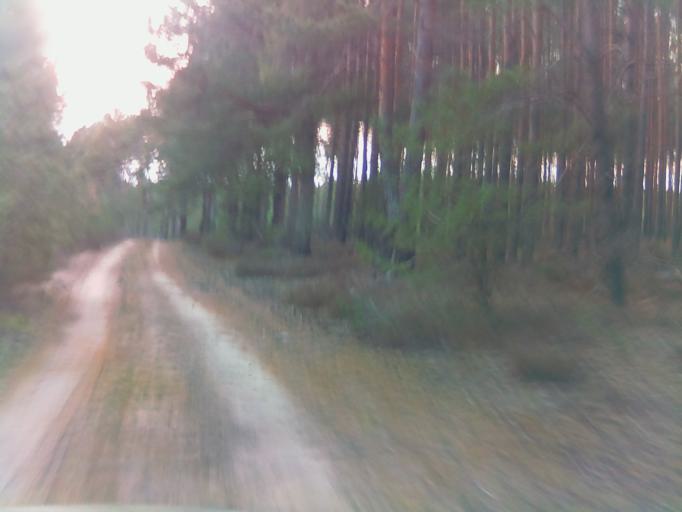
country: DE
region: Brandenburg
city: Jamlitz
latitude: 51.9693
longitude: 14.4208
